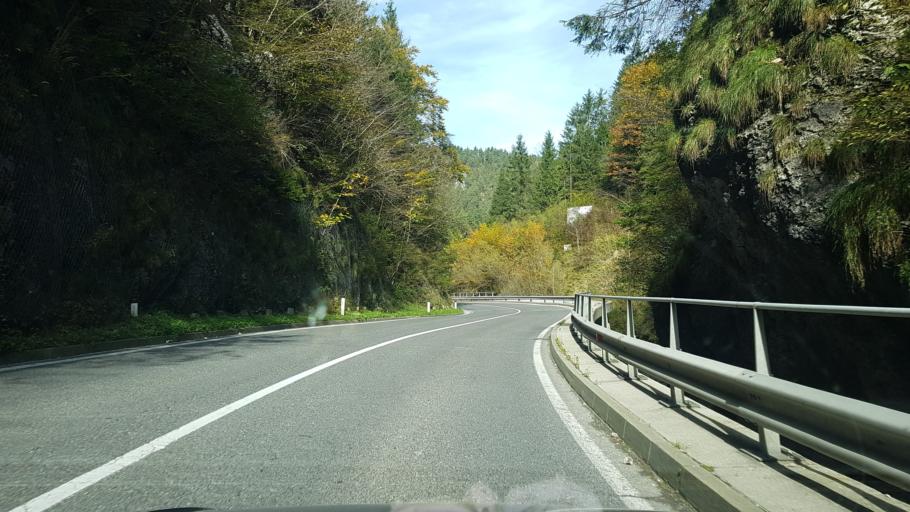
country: SI
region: Velenje
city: Velenje
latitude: 46.4170
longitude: 15.1740
